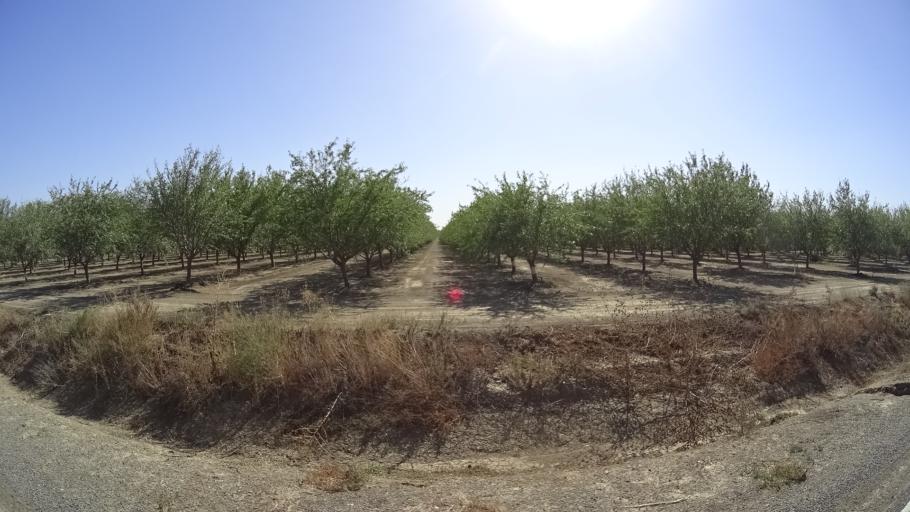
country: US
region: California
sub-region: Yolo County
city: Davis
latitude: 38.5905
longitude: -121.8189
